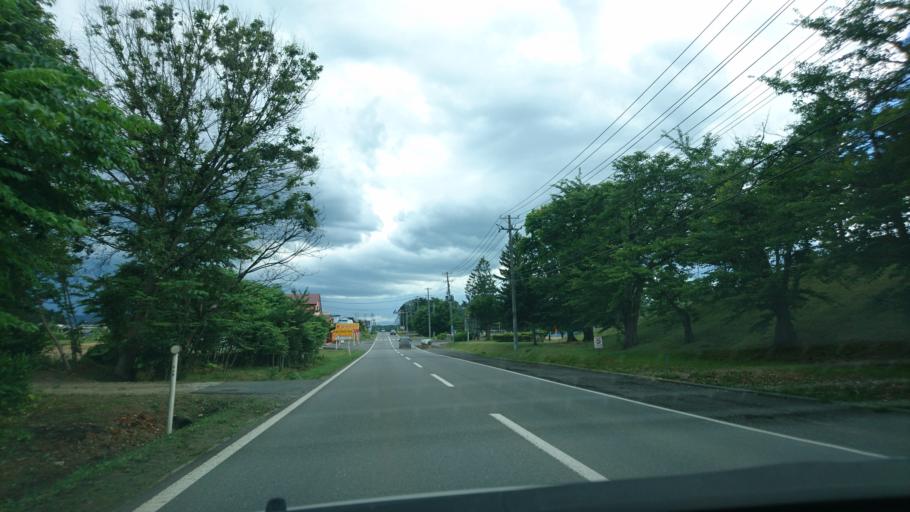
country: JP
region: Iwate
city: Kitakami
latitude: 39.3280
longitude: 141.1277
